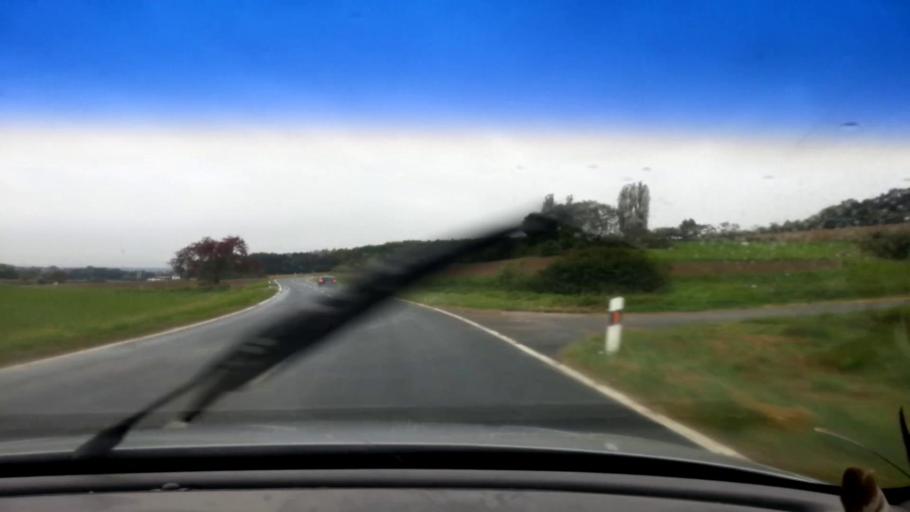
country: DE
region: Bavaria
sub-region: Upper Franconia
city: Schesslitz
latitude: 49.9809
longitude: 11.0762
